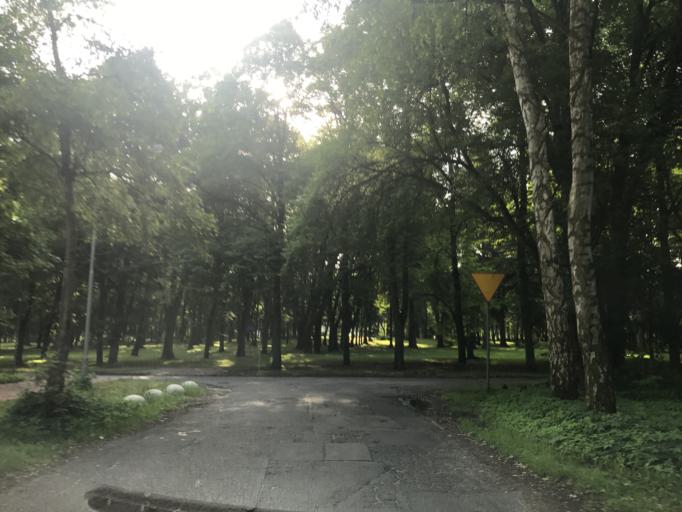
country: PL
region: West Pomeranian Voivodeship
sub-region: Powiat goleniowski
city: Goleniow
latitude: 53.5577
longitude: 14.8191
